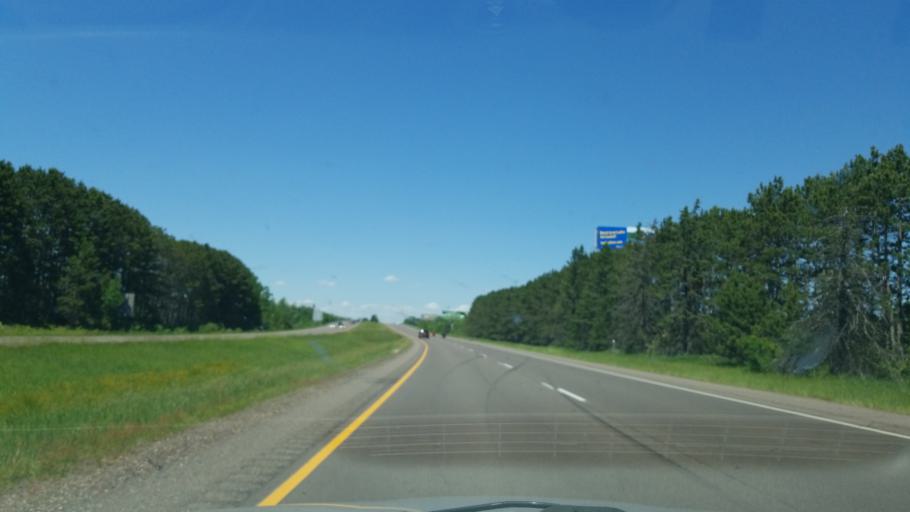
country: US
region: Minnesota
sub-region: Pine County
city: Hinckley
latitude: 46.0263
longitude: -92.9250
